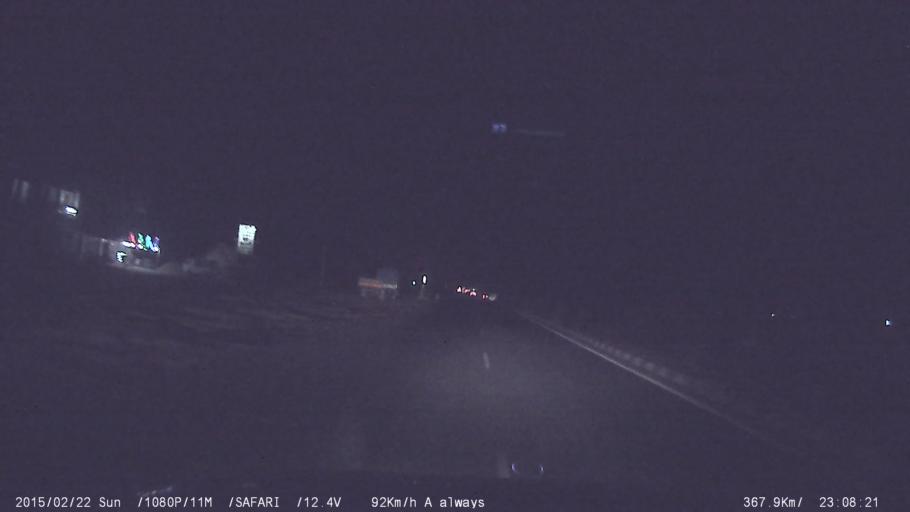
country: IN
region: Tamil Nadu
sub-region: Namakkal
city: Rasipuram
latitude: 11.4517
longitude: 78.1588
